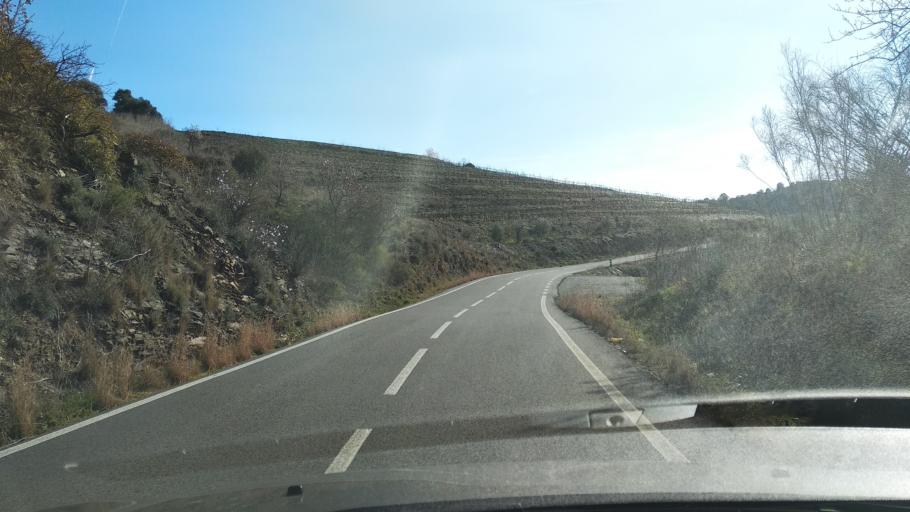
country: ES
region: Catalonia
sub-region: Provincia de Tarragona
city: el Masroig
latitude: 41.1834
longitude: 0.7460
